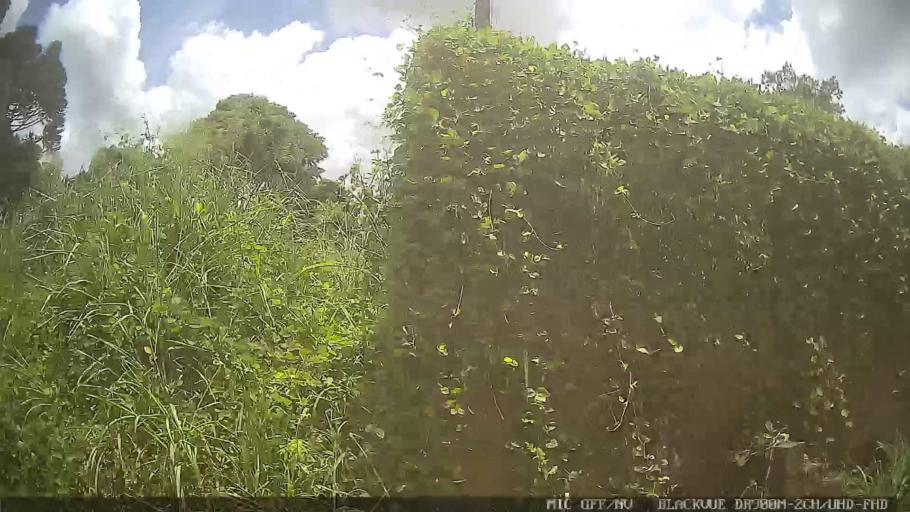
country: BR
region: Sao Paulo
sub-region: Braganca Paulista
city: Braganca Paulista
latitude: -23.0292
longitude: -46.5276
